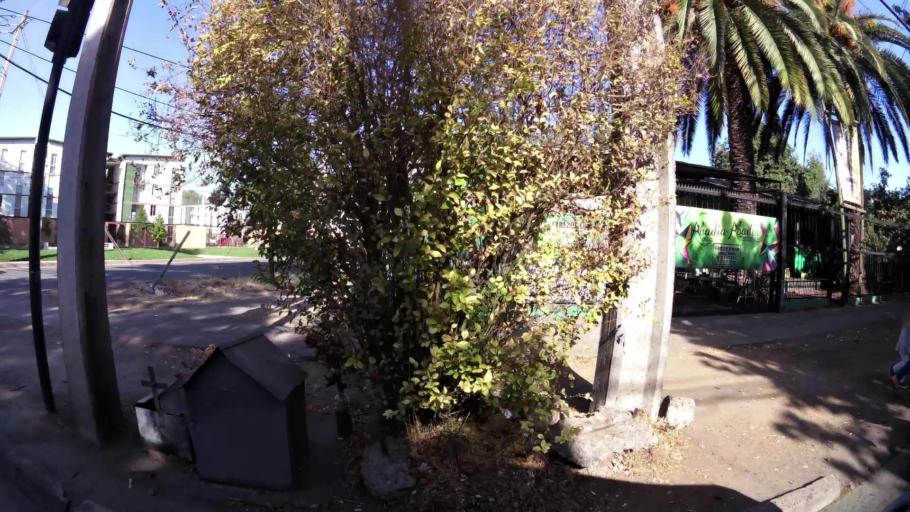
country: CL
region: Maule
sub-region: Provincia de Talca
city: Talca
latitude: -35.4368
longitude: -71.6662
